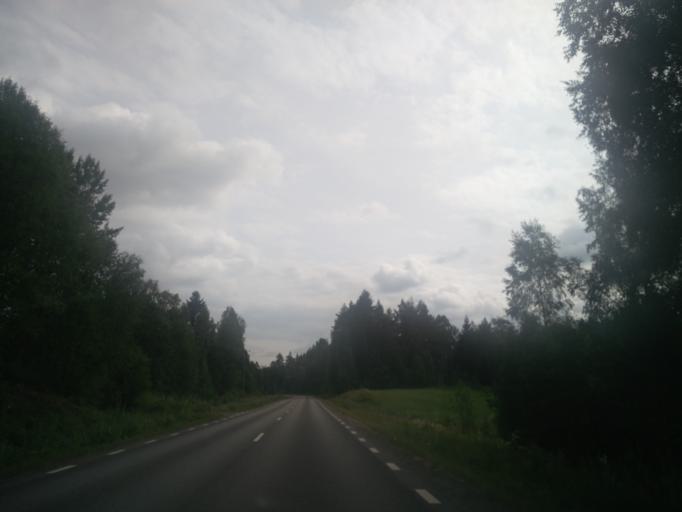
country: SE
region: Vaermland
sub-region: Arvika Kommun
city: Arvika
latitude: 59.7202
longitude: 12.5680
